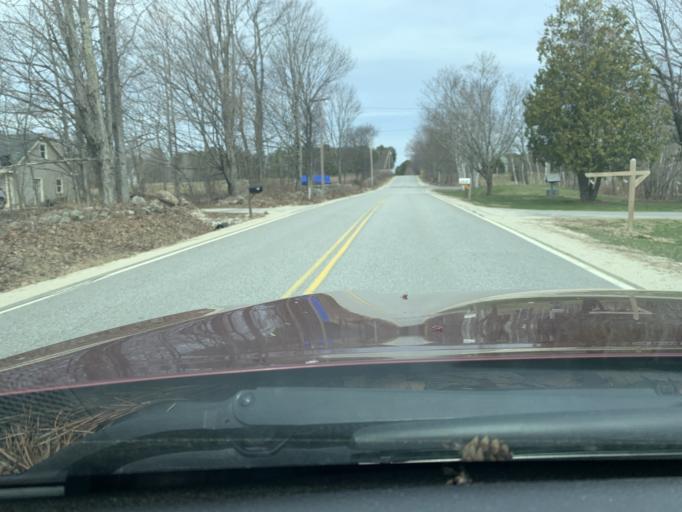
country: US
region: Maine
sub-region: Androscoggin County
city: Poland
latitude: 43.9622
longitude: -70.3911
